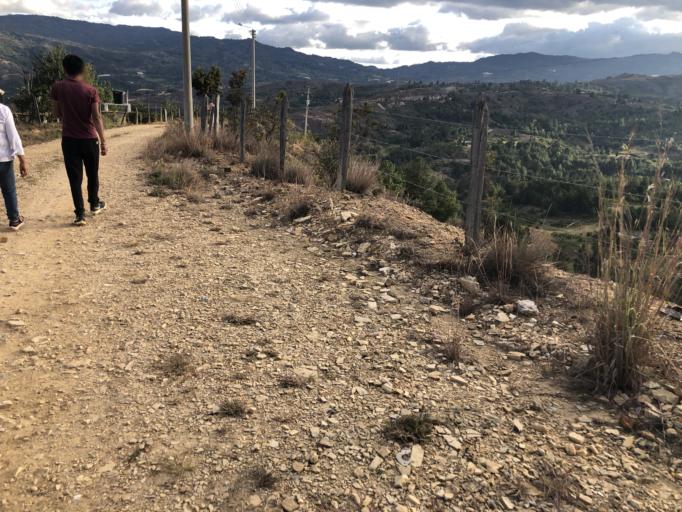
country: CO
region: Boyaca
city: Raquira
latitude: 5.5786
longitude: -73.6593
